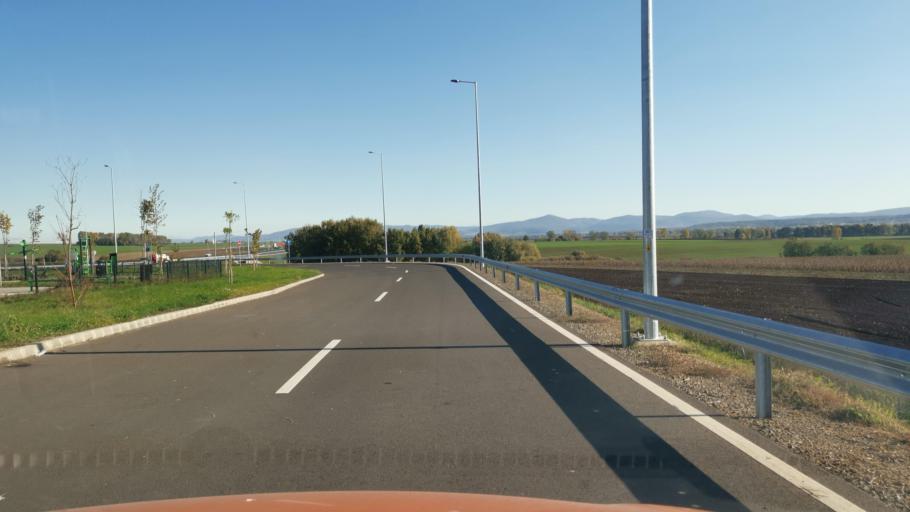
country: HU
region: Borsod-Abauj-Zemplen
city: Halmaj
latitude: 48.2891
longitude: 21.0276
